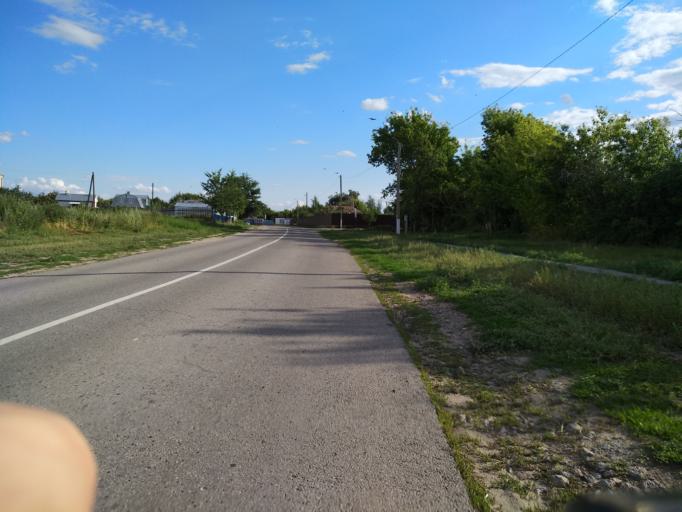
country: RU
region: Lipetsk
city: Dobrinka
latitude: 52.0390
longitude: 40.5535
